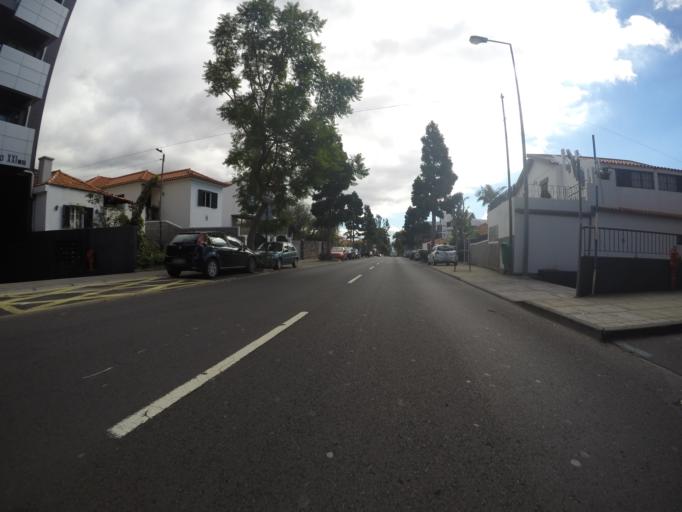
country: PT
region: Madeira
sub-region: Funchal
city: Nossa Senhora do Monte
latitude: 32.6583
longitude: -16.9274
